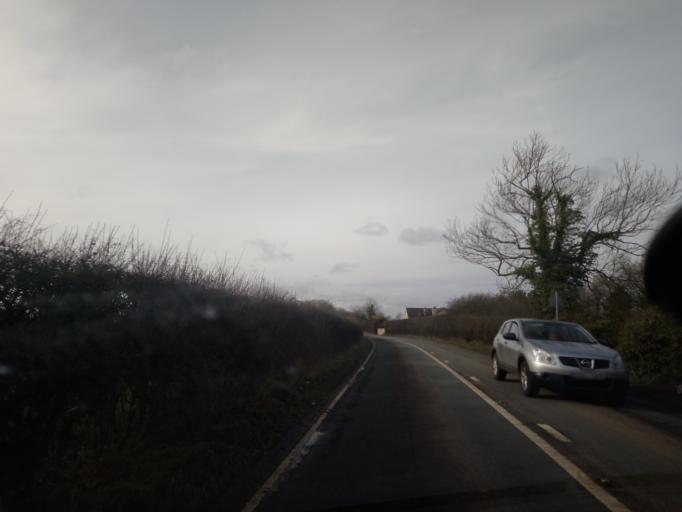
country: GB
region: England
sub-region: Shropshire
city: Prees
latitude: 52.8757
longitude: -2.6146
